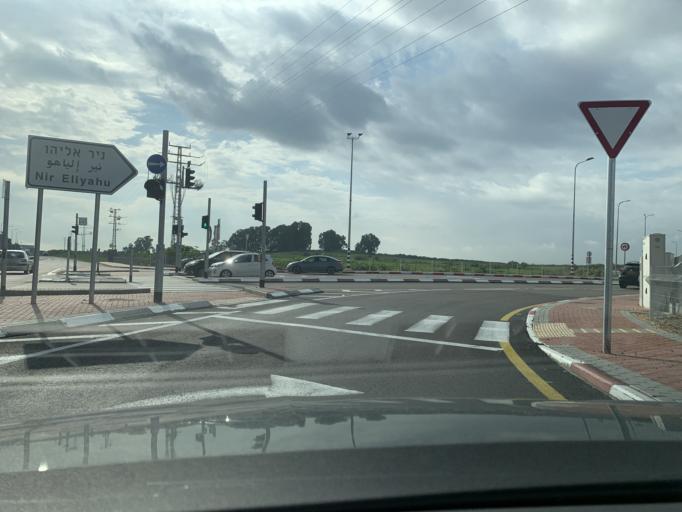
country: PS
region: West Bank
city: Qalqilyah
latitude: 32.1932
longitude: 34.9532
